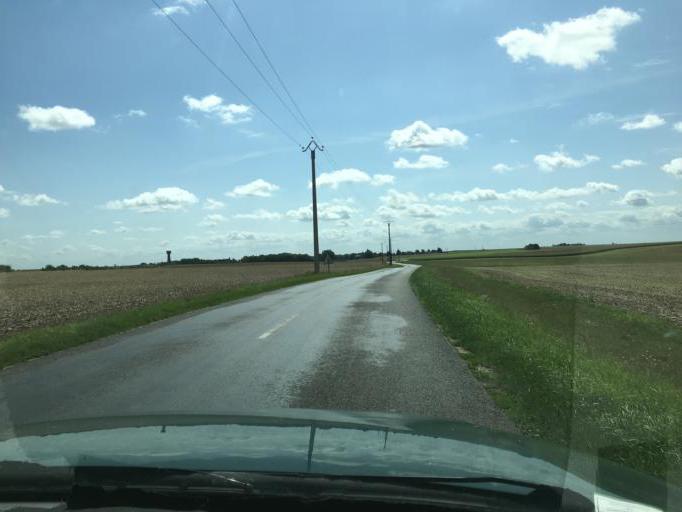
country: FR
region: Centre
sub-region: Departement du Loiret
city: Patay
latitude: 48.0193
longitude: 1.7283
